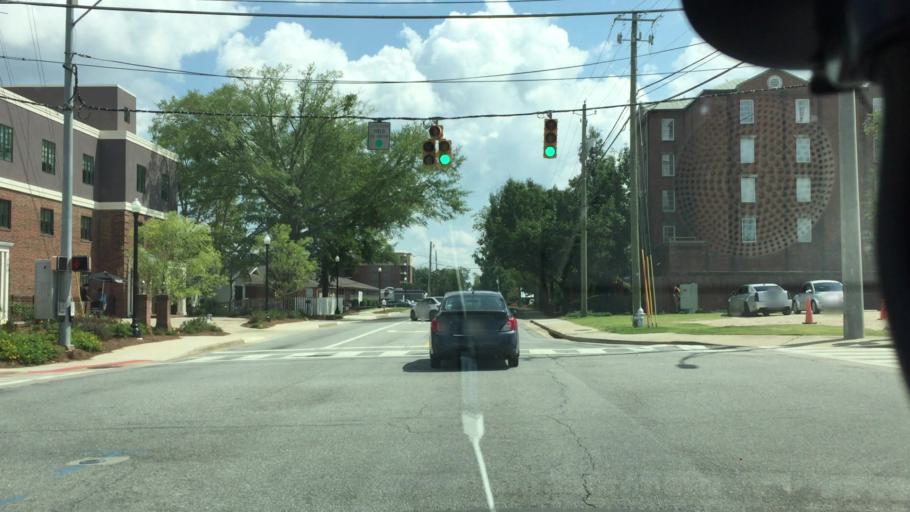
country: US
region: Alabama
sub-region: Lee County
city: Auburn
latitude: 32.6043
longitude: -85.4799
